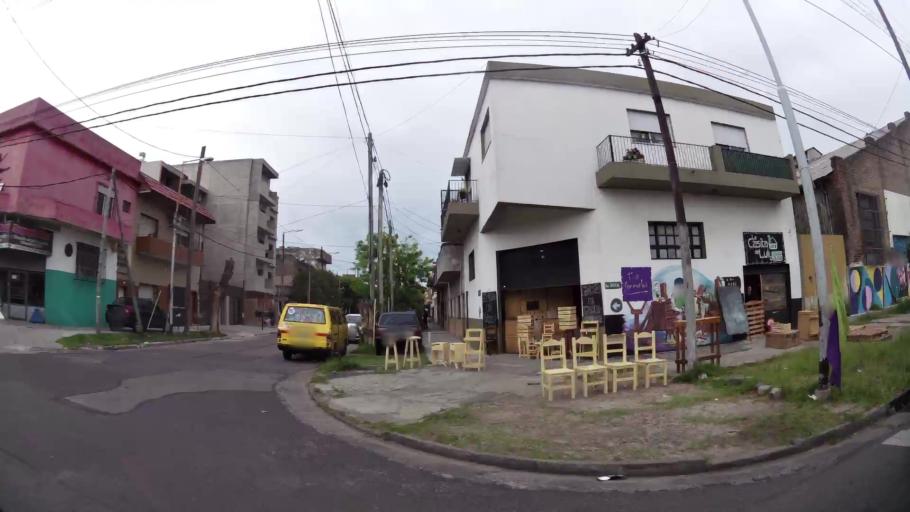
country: AR
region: Buenos Aires
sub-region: Partido de Avellaneda
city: Avellaneda
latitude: -34.6707
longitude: -58.3483
